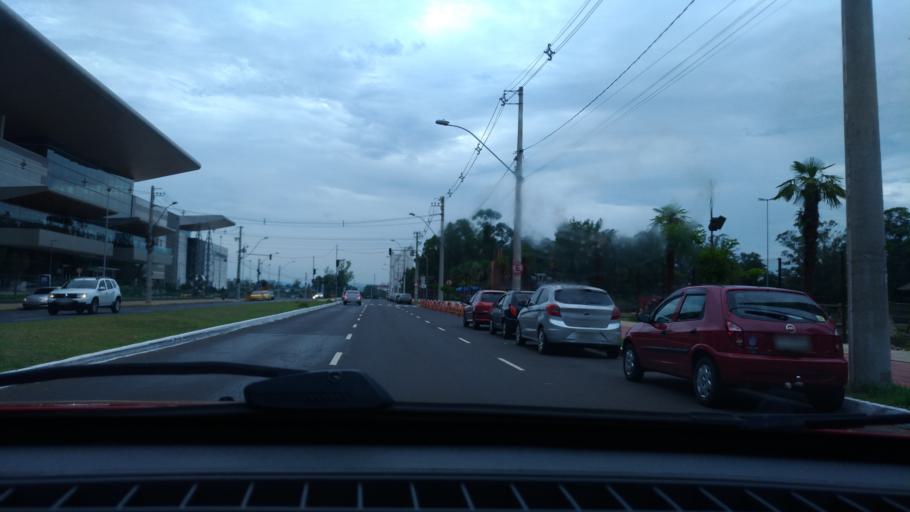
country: BR
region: Rio Grande do Sul
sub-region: Canoas
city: Canoas
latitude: -29.9141
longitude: -51.1658
